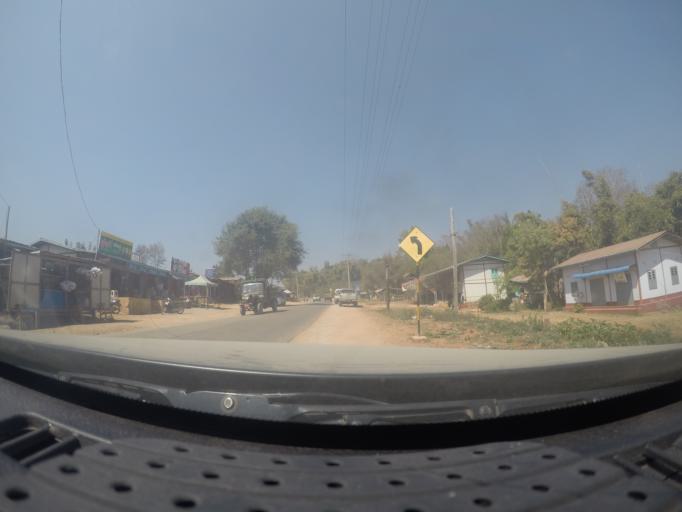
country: MM
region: Shan
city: Taunggyi
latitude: 20.7898
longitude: 96.6494
